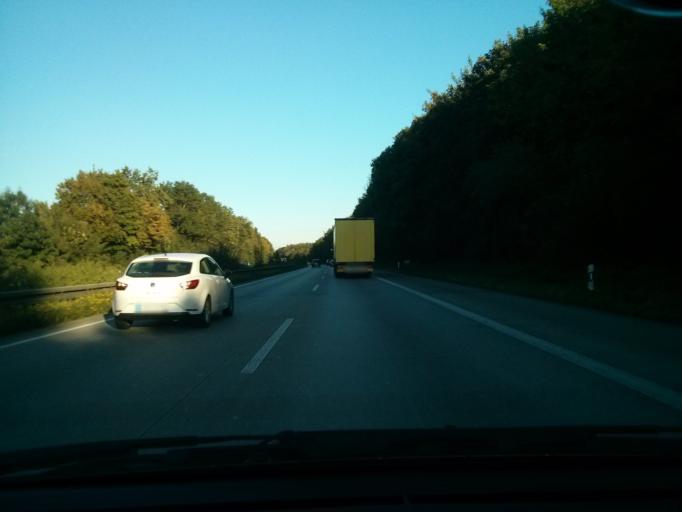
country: DE
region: North Rhine-Westphalia
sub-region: Regierungsbezirk Arnsberg
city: Frondenberg
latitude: 51.5245
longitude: 7.7759
